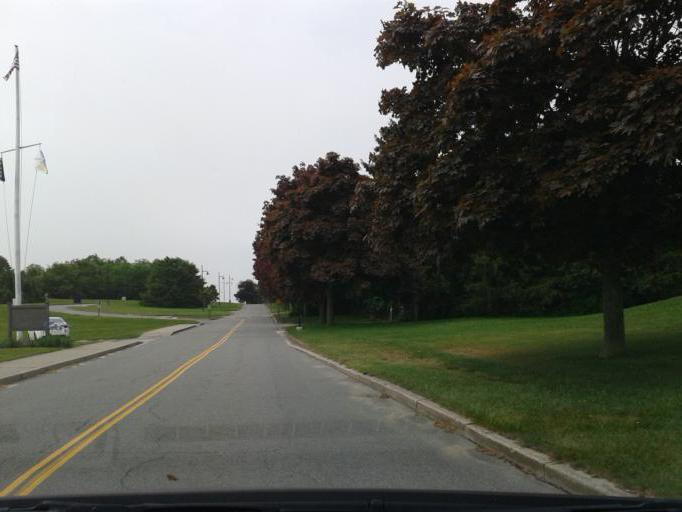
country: US
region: Rhode Island
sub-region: Newport County
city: Newport
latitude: 41.4724
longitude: -71.3386
